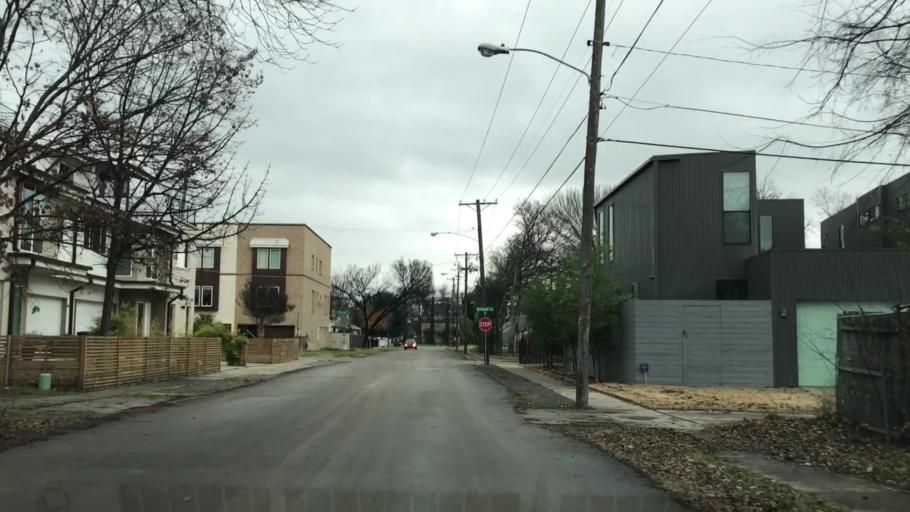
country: US
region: Texas
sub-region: Dallas County
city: Highland Park
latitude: 32.8110
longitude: -96.7856
